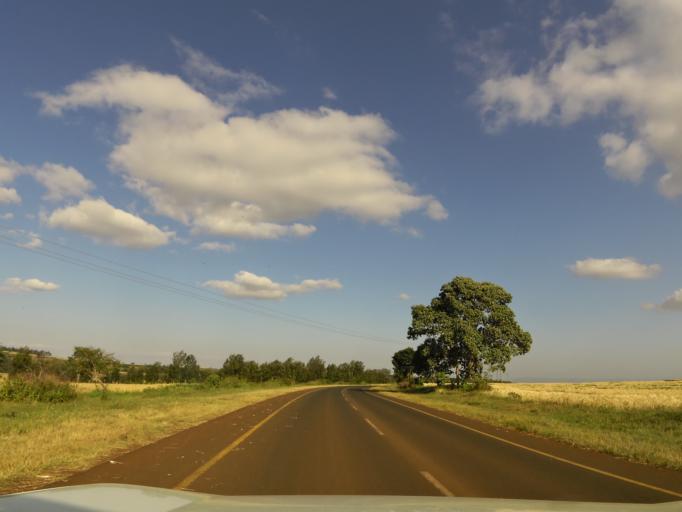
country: TZ
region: Arusha
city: Kiratu
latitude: -3.3170
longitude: 35.5965
